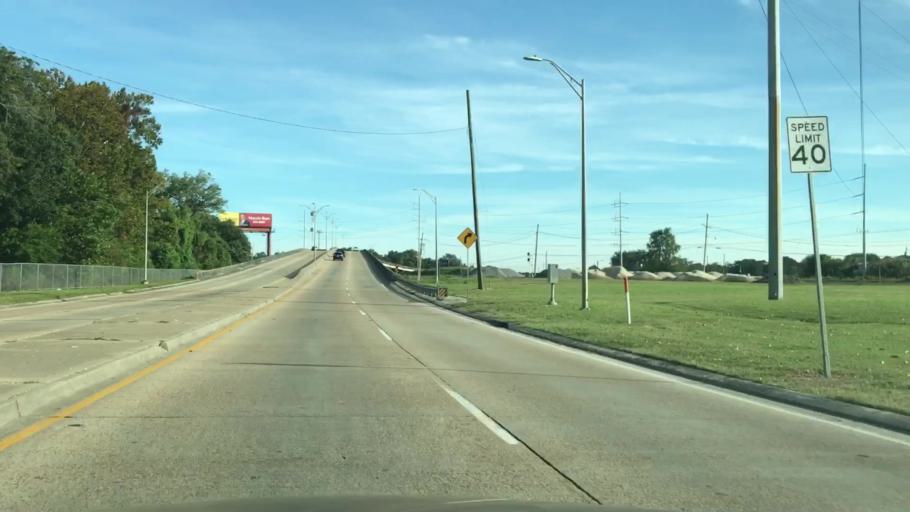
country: US
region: Louisiana
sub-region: Jefferson Parish
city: River Ridge
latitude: 29.9753
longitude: -90.2090
